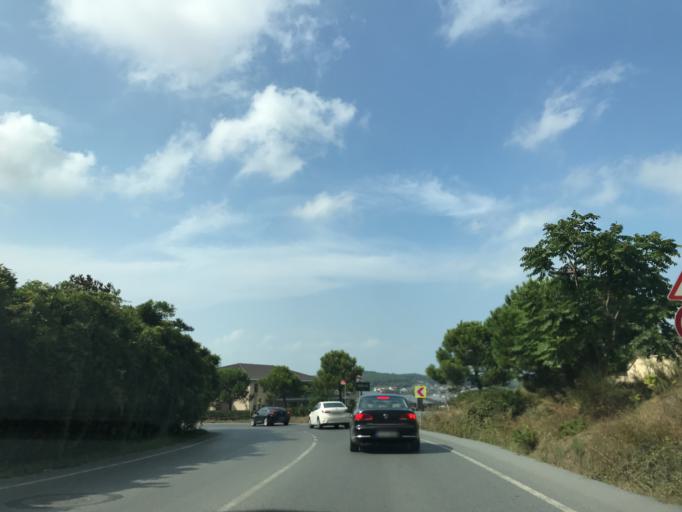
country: TR
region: Istanbul
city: Arikoey
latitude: 41.2128
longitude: 29.0355
